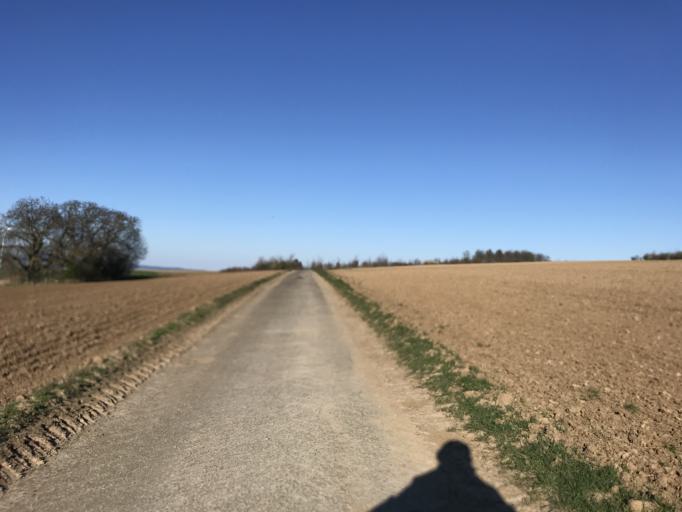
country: DE
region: Rheinland-Pfalz
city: Klein-Winternheim
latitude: 49.9243
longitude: 8.2314
